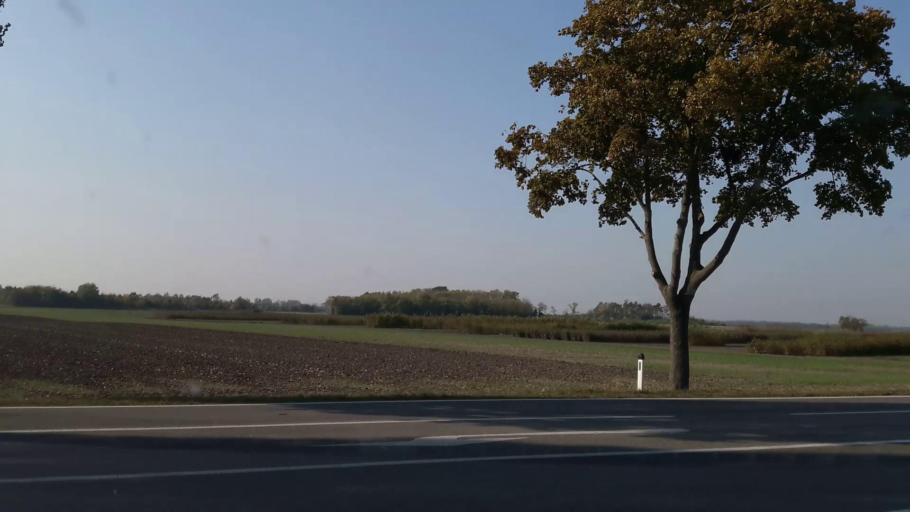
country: AT
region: Lower Austria
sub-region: Politischer Bezirk Ganserndorf
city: Engelhartstetten
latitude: 48.1999
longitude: 16.9011
